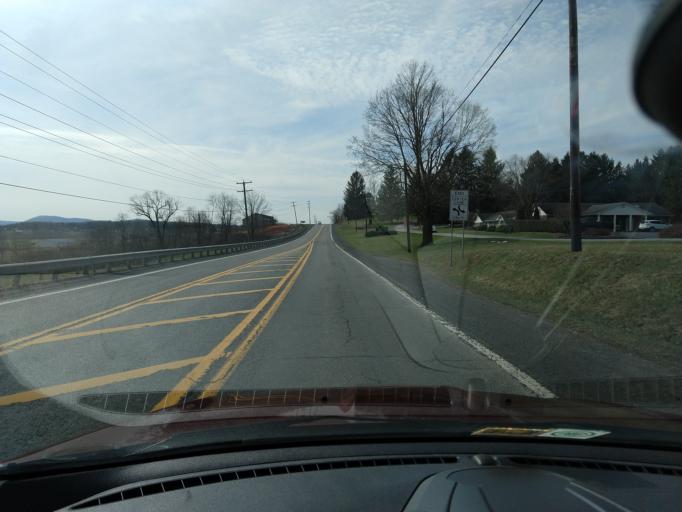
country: US
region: West Virginia
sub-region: Greenbrier County
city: Lewisburg
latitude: 37.8442
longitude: -80.4148
